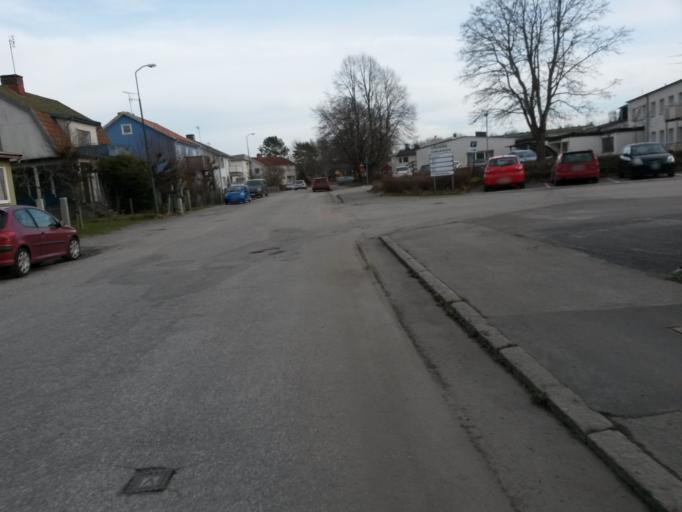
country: SE
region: Vaestra Goetaland
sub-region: Herrljunga Kommun
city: Herrljunga
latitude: 58.0777
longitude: 13.0289
